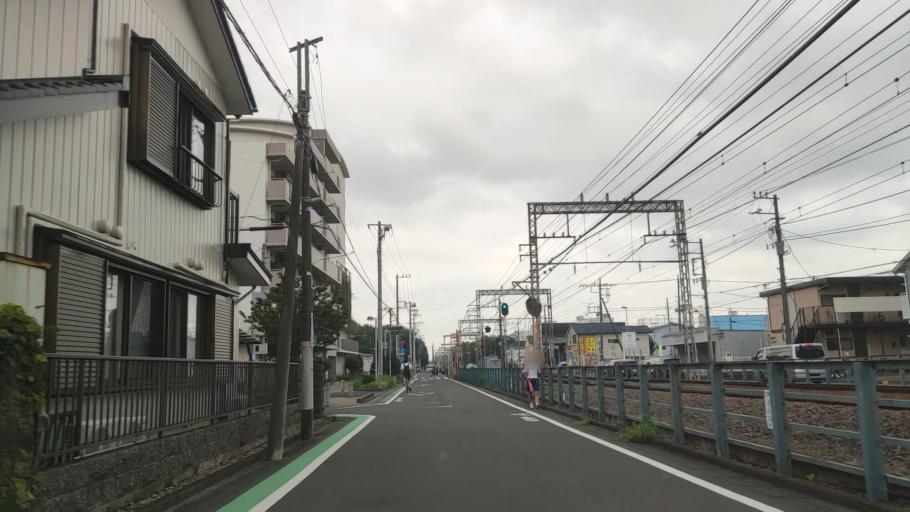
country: JP
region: Kanagawa
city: Minami-rinkan
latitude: 35.4864
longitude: 139.4529
